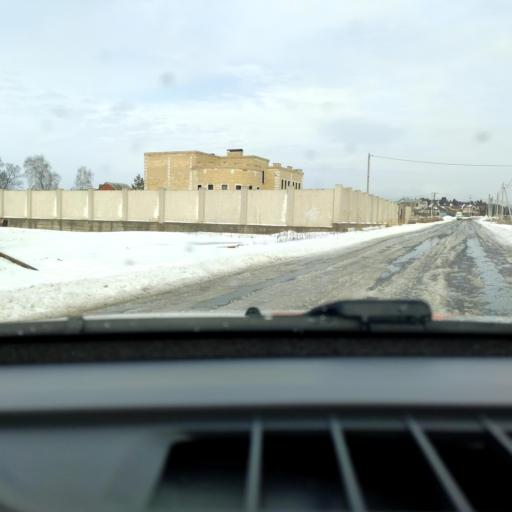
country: RU
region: Voronezj
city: Podgornoye
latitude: 51.7723
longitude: 39.1239
